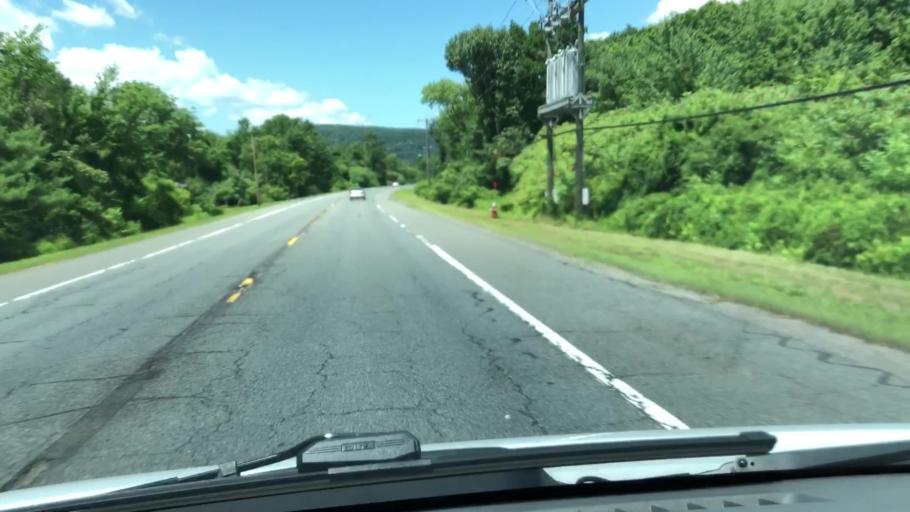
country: US
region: Massachusetts
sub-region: Franklin County
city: South Deerfield
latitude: 42.4589
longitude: -72.5706
